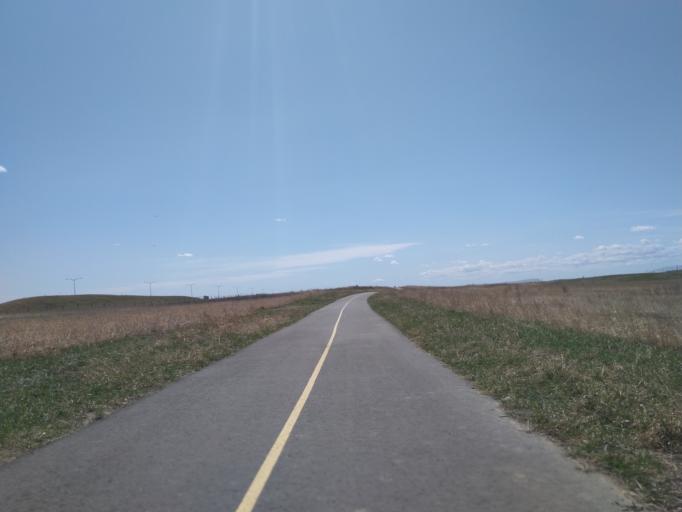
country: CA
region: Alberta
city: Chestermere
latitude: 51.0334
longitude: -113.9237
